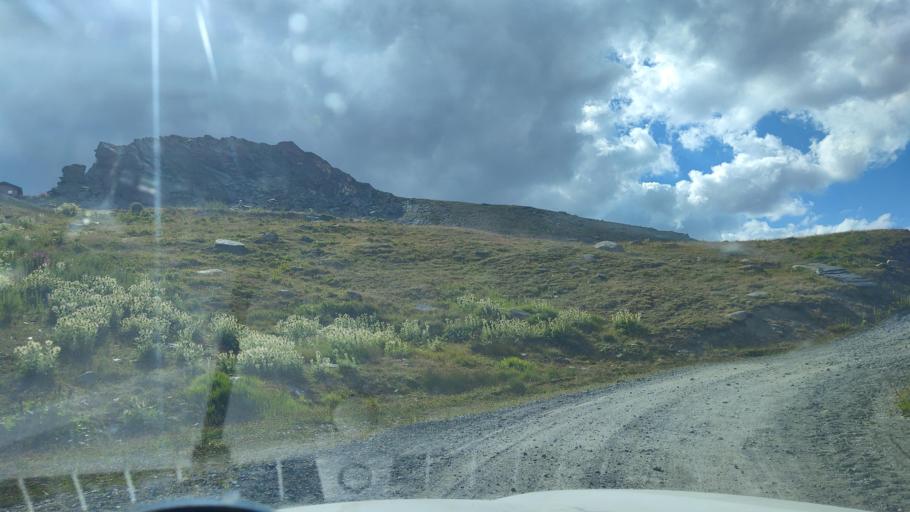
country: FR
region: Rhone-Alpes
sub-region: Departement de la Savoie
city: Val Thorens
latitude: 45.2777
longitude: 6.5816
